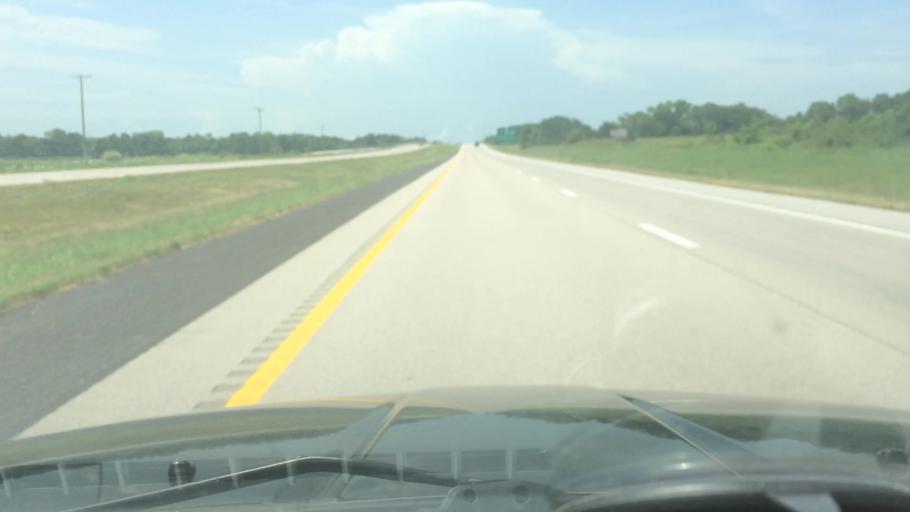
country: US
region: Missouri
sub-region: Polk County
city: Humansville
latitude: 37.7899
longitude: -93.5843
